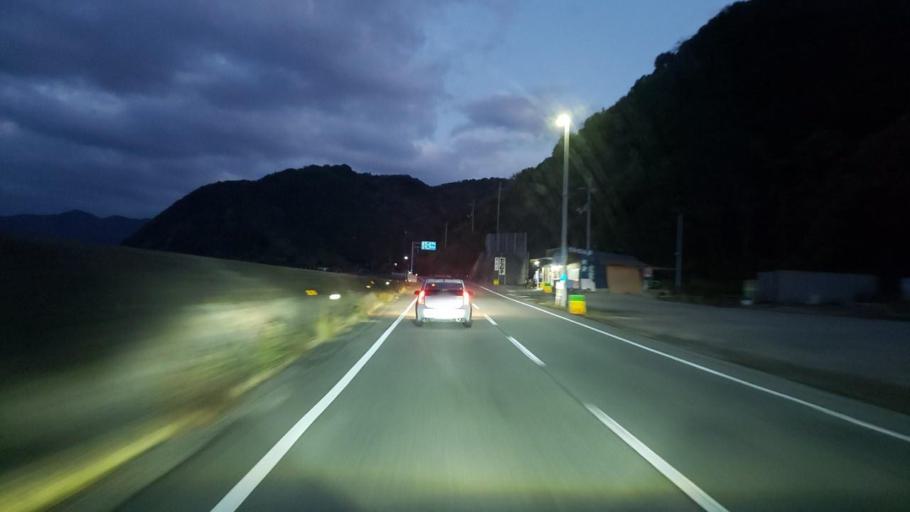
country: JP
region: Tokushima
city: Ishii
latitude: 34.2061
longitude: 134.4473
